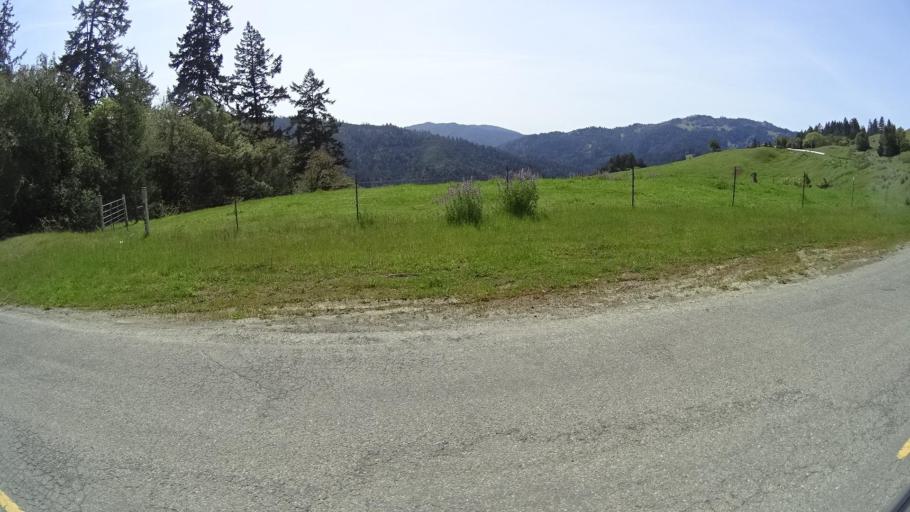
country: US
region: California
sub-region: Humboldt County
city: Redway
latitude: 40.4044
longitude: -123.7462
